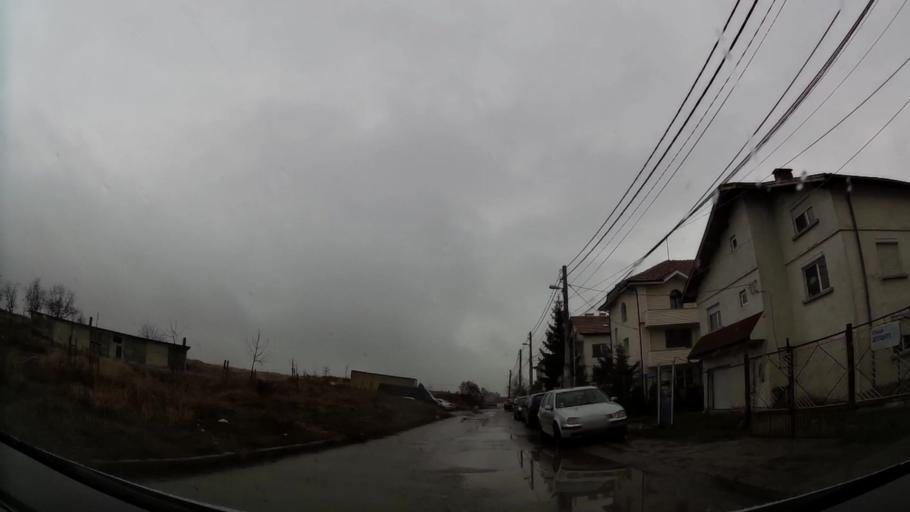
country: BG
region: Sofia-Capital
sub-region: Stolichna Obshtina
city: Sofia
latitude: 42.6319
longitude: 23.4048
